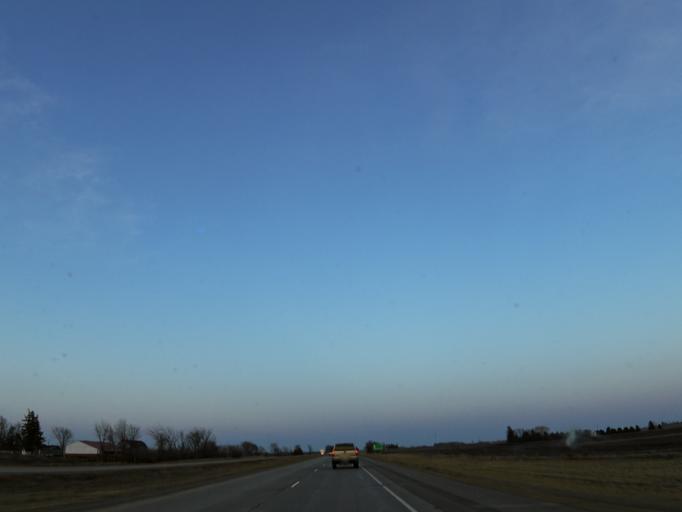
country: US
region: Minnesota
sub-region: Mower County
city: Austin
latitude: 43.6722
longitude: -92.8559
